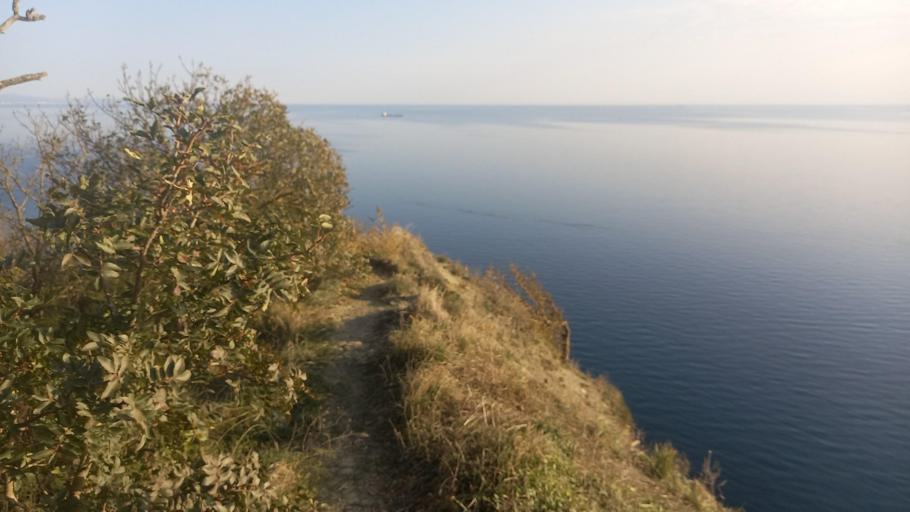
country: RU
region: Krasnodarskiy
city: Abrau-Dyurso
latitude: 44.6711
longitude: 37.5843
